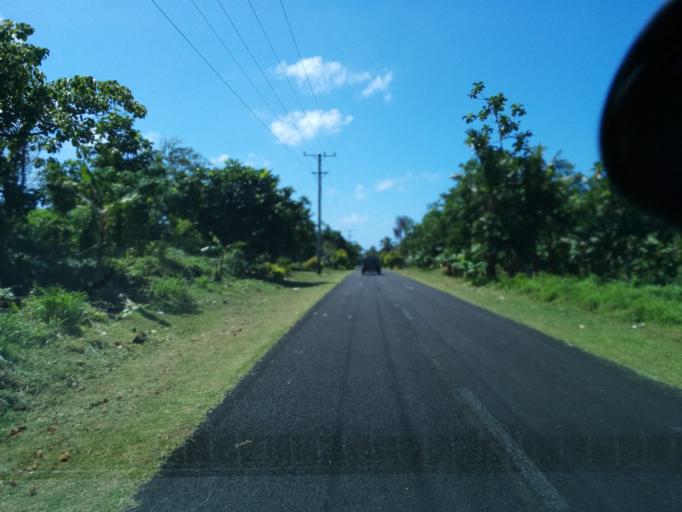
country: WS
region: Gagaifomauga
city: Safotu
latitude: -13.5190
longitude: -172.2704
